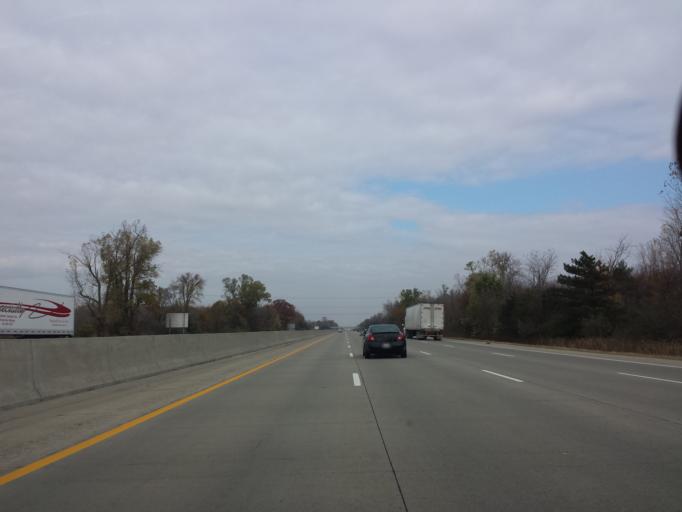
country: US
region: Michigan
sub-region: Genesee County
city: Clio
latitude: 43.1957
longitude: -83.7689
